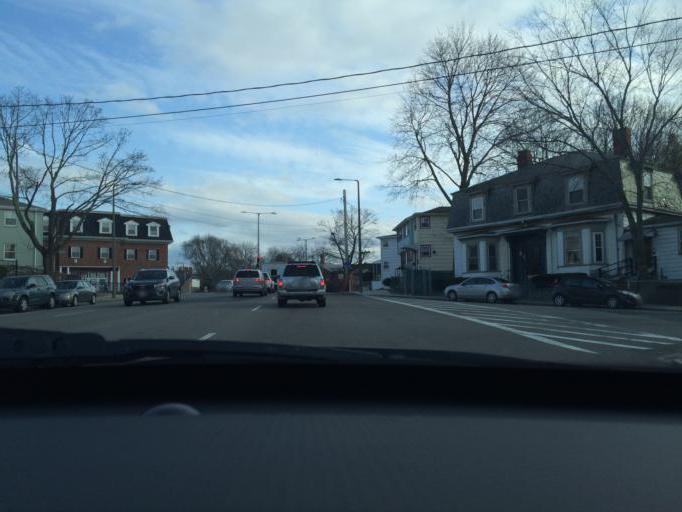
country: US
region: Massachusetts
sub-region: Norfolk County
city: Milton
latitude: 42.2743
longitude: -71.0711
